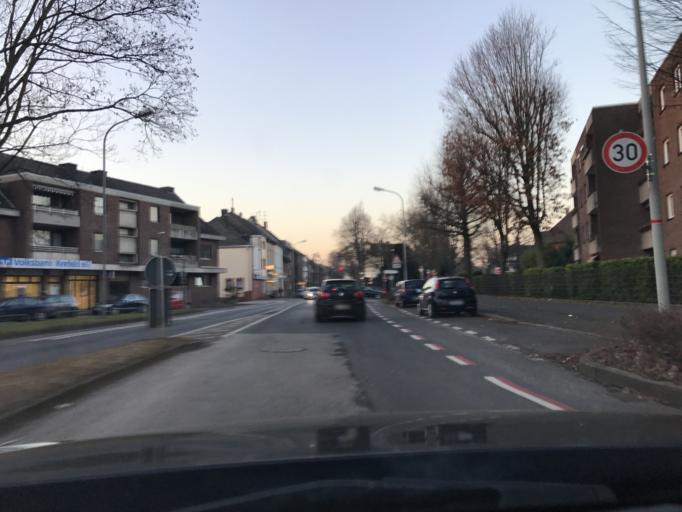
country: DE
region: North Rhine-Westphalia
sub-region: Regierungsbezirk Dusseldorf
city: Krefeld
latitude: 51.3316
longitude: 6.6124
